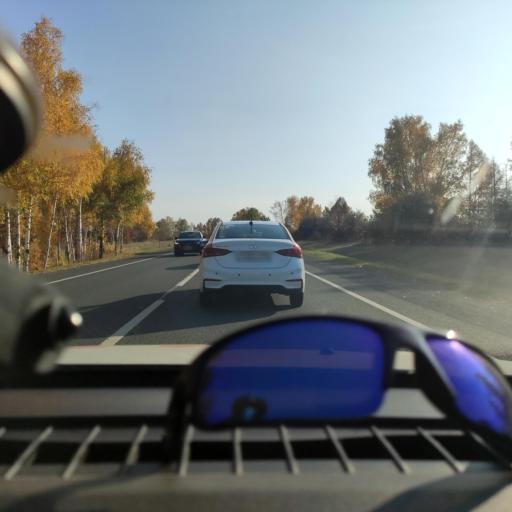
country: RU
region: Samara
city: Bereza
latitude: 53.4795
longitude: 50.1166
